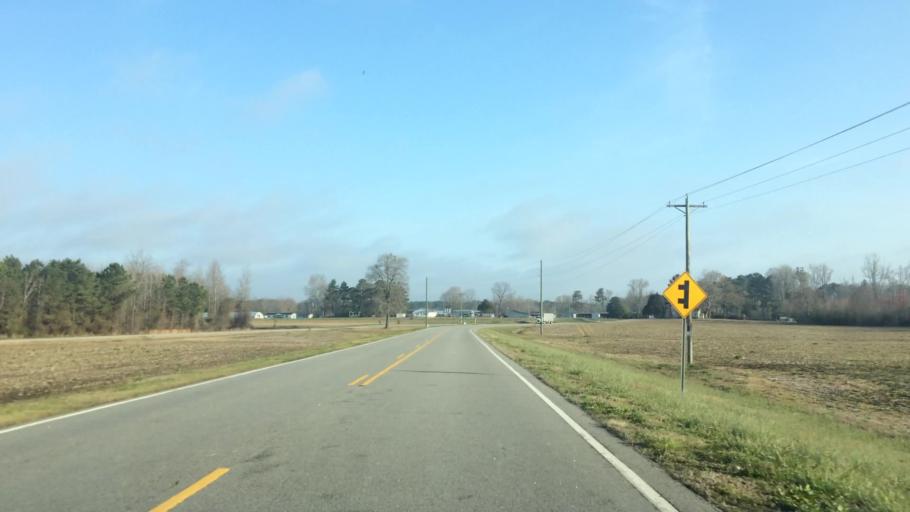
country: US
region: North Carolina
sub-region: Edgecombe County
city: Pinetops
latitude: 35.7258
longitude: -77.6354
